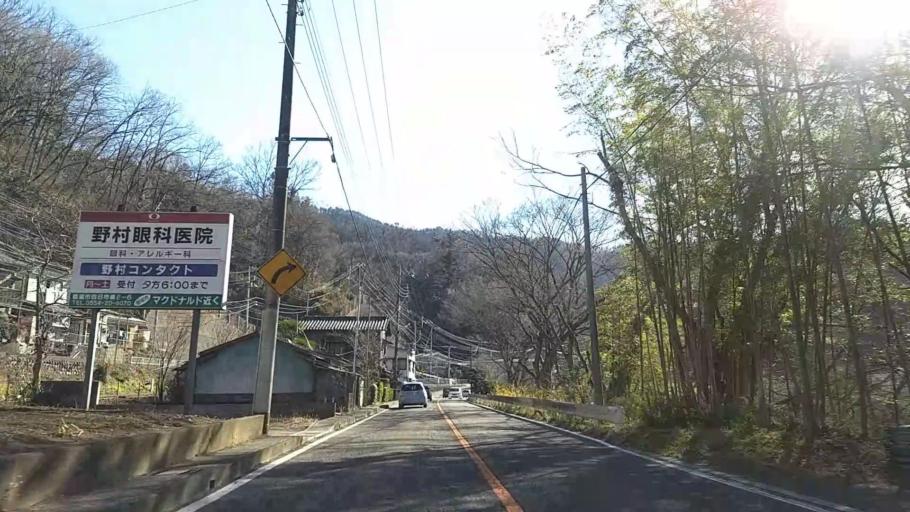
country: JP
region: Yamanashi
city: Otsuki
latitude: 35.6055
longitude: 138.9411
